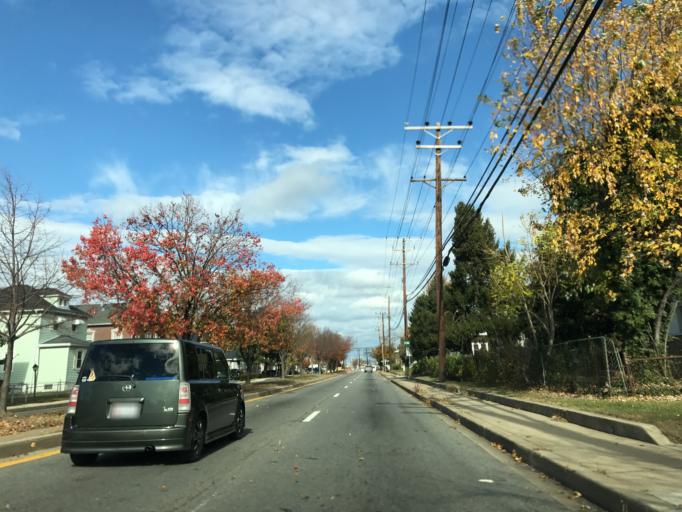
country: US
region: Maryland
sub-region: Anne Arundel County
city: Brooklyn Park
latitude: 39.2276
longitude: -76.6132
